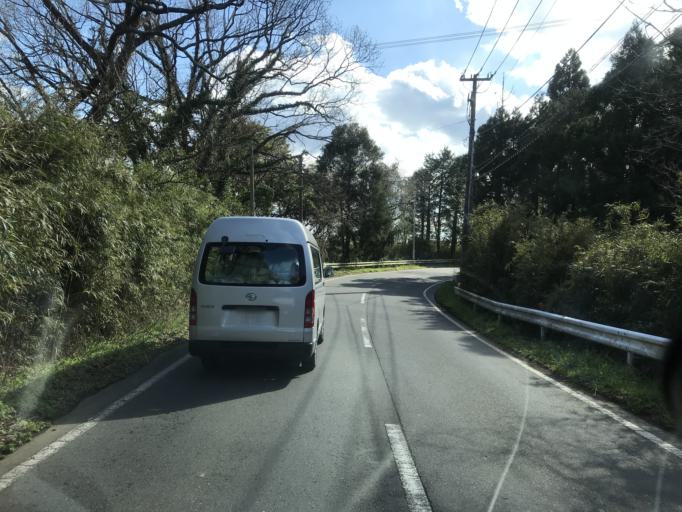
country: JP
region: Chiba
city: Sawara
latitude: 35.8669
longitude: 140.4197
